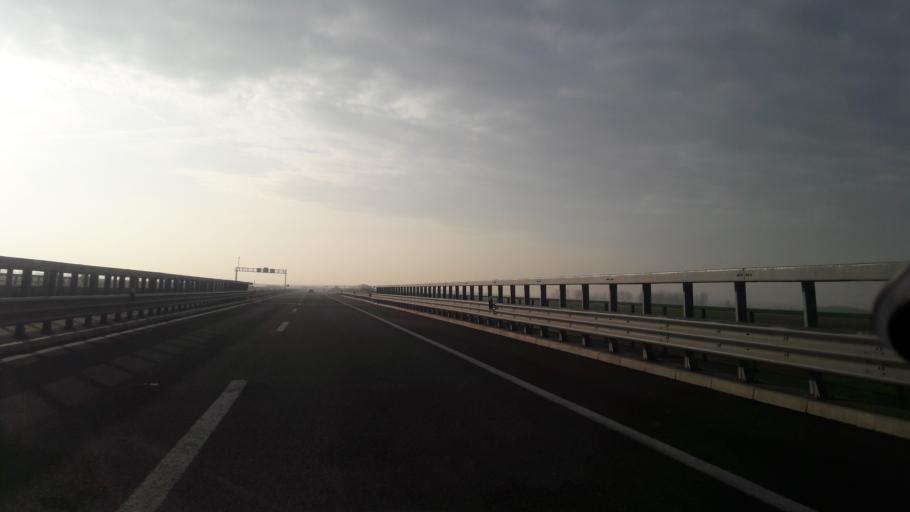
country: HR
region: Osjecko-Baranjska
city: Gorjani
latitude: 45.3644
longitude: 18.3973
